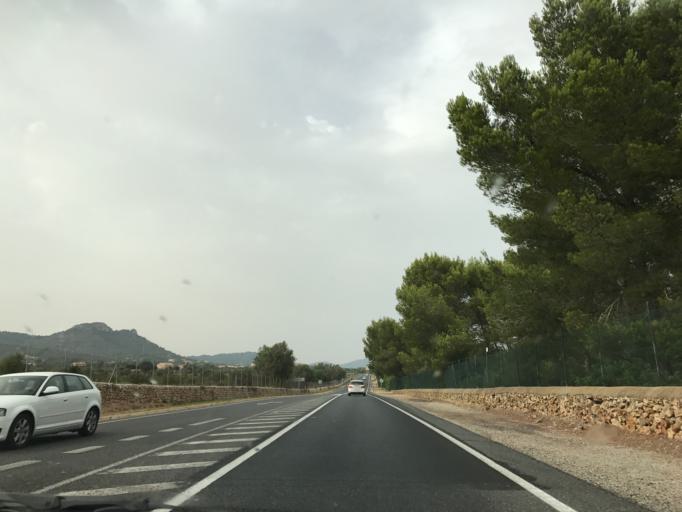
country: ES
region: Balearic Islands
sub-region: Illes Balears
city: Son Servera
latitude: 39.5845
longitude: 3.3646
